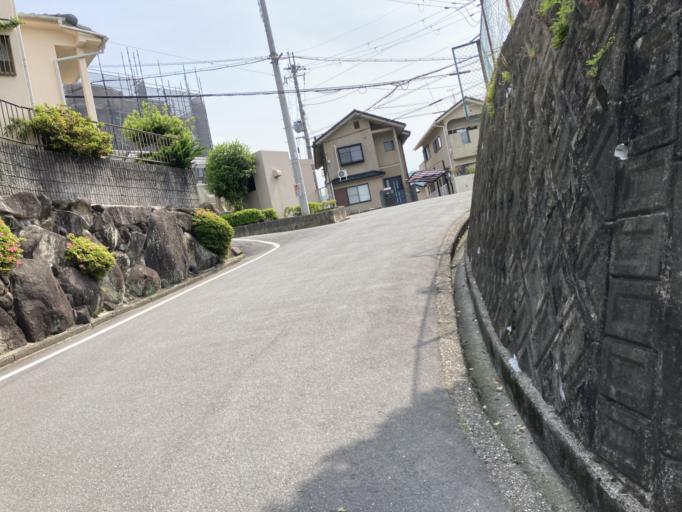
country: JP
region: Nara
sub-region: Ikoma-shi
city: Ikoma
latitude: 34.7103
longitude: 135.6962
